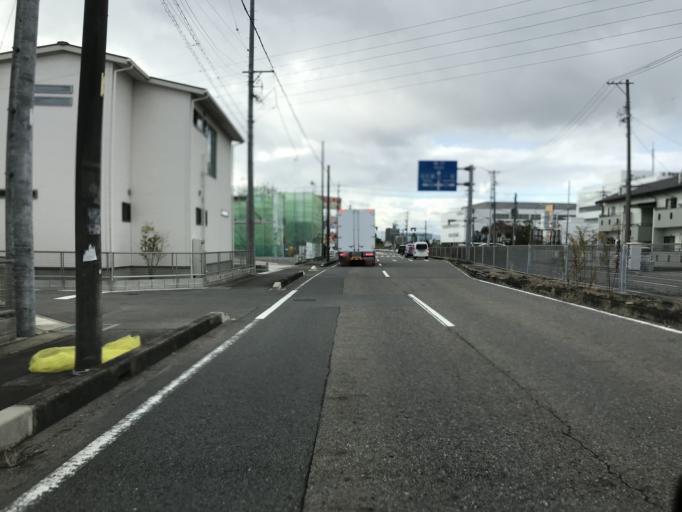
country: JP
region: Aichi
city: Inazawa
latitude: 35.2375
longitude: 136.8350
